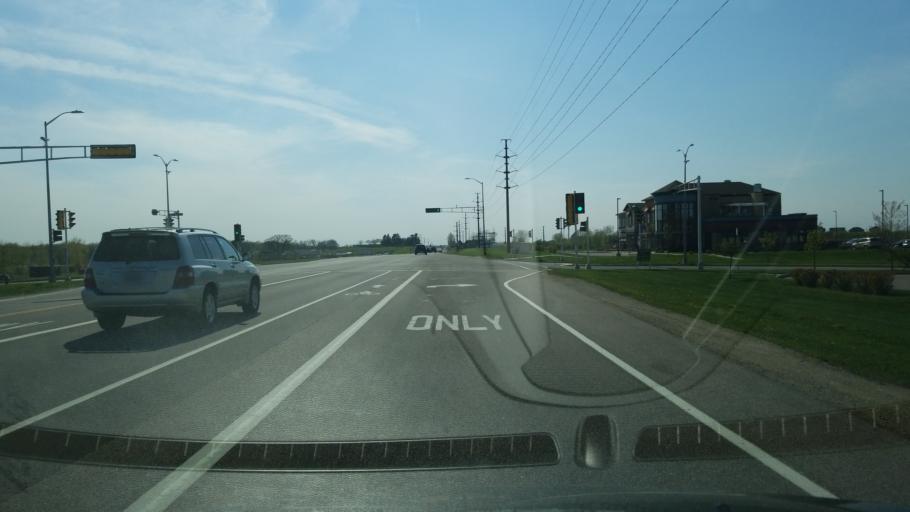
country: US
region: Wisconsin
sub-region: Dane County
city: Verona
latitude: 42.9724
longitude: -89.5062
